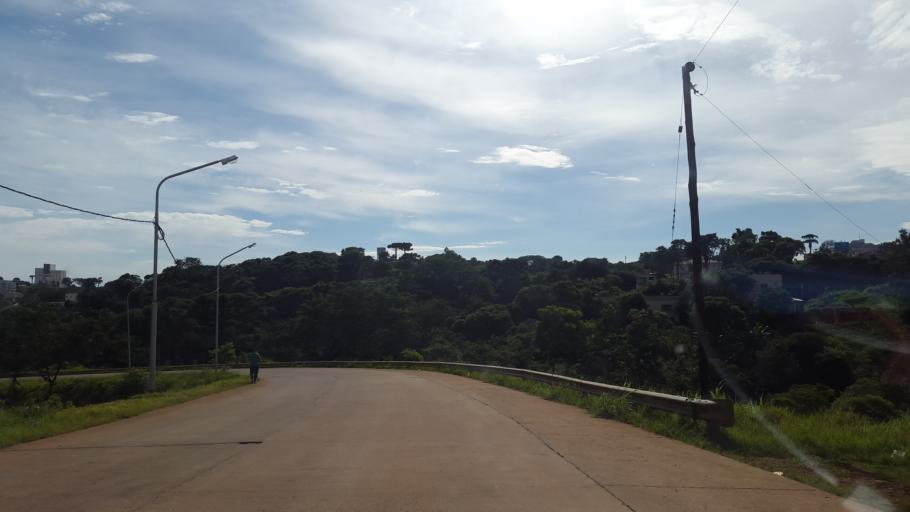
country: AR
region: Misiones
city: Bernardo de Irigoyen
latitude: -26.2604
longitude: -53.6433
